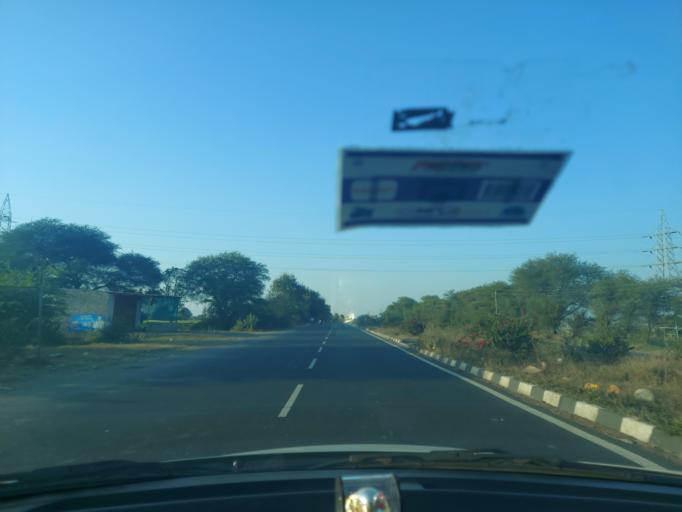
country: IN
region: Madhya Pradesh
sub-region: Indore
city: Sanwer
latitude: 23.0560
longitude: 75.8252
